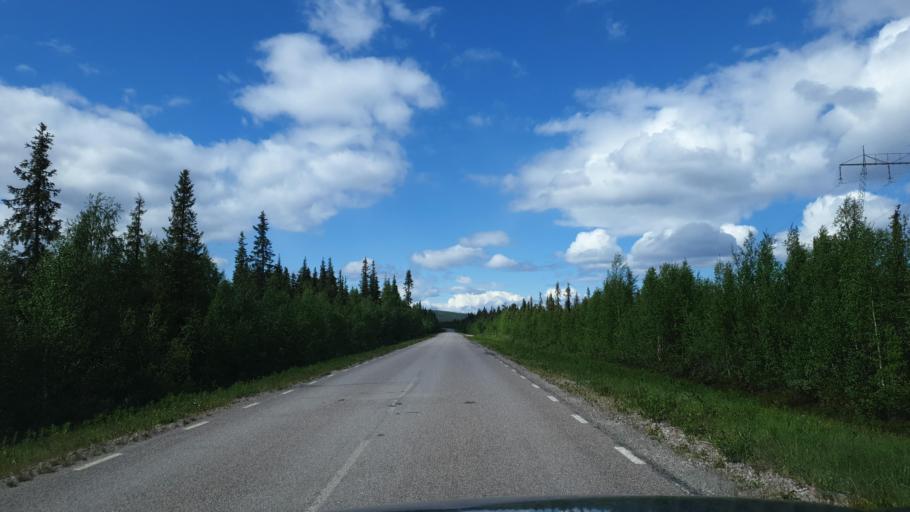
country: SE
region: Norrbotten
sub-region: Jokkmokks Kommun
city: Jokkmokk
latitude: 67.0926
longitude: 19.7563
